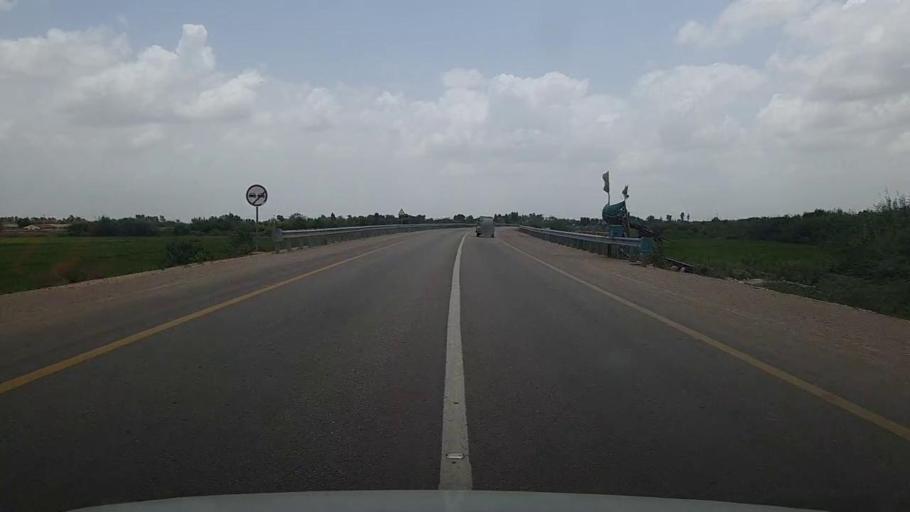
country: PK
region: Sindh
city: Thatta
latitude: 24.7507
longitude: 67.9528
